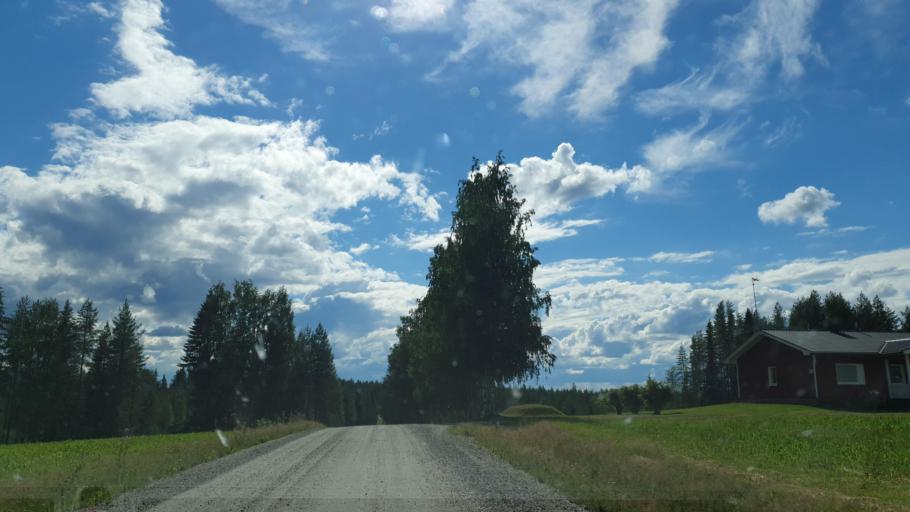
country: FI
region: Kainuu
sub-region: Kehys-Kainuu
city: Kuhmo
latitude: 64.1486
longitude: 29.7863
